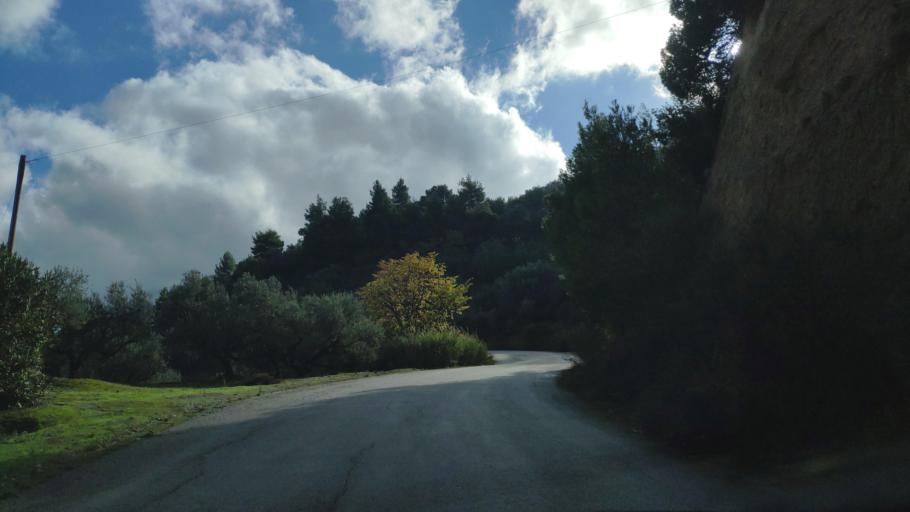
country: GR
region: West Greece
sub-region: Nomos Achaias
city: Aiyira
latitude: 38.1026
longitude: 22.4438
